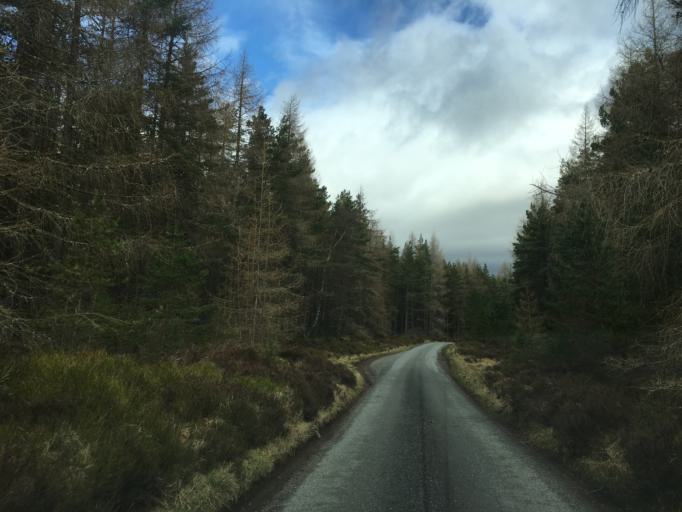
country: GB
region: Scotland
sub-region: Highland
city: Kingussie
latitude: 57.0986
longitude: -3.9208
